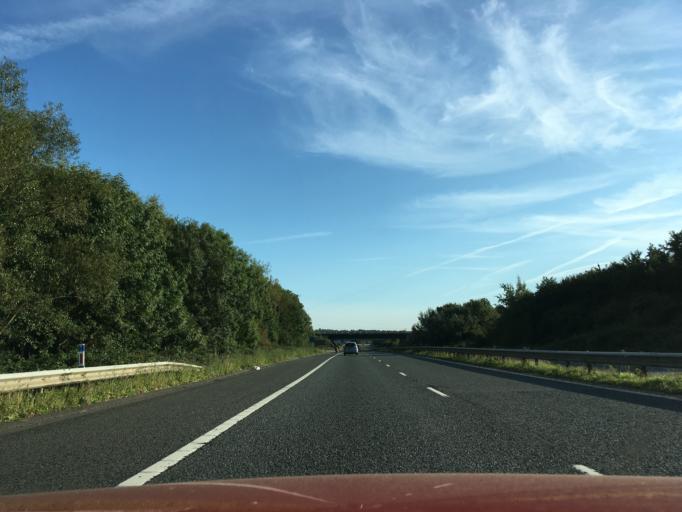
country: GB
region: England
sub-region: South Gloucestershire
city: Severn Beach
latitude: 51.5204
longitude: -2.6600
